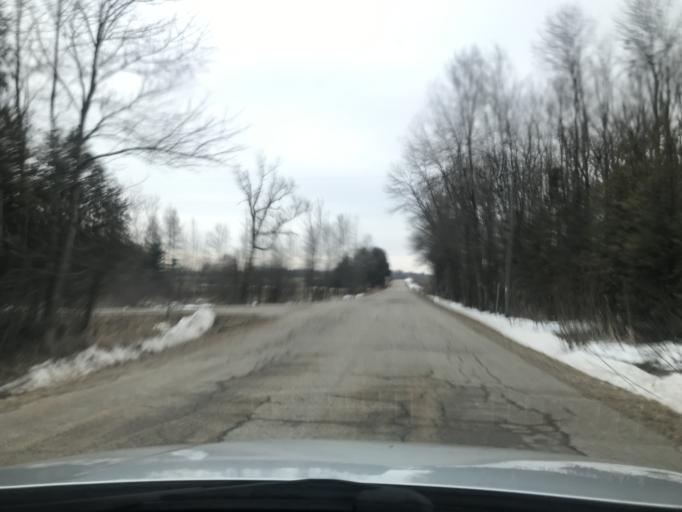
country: US
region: Wisconsin
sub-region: Marinette County
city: Peshtigo
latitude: 45.1164
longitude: -88.0081
